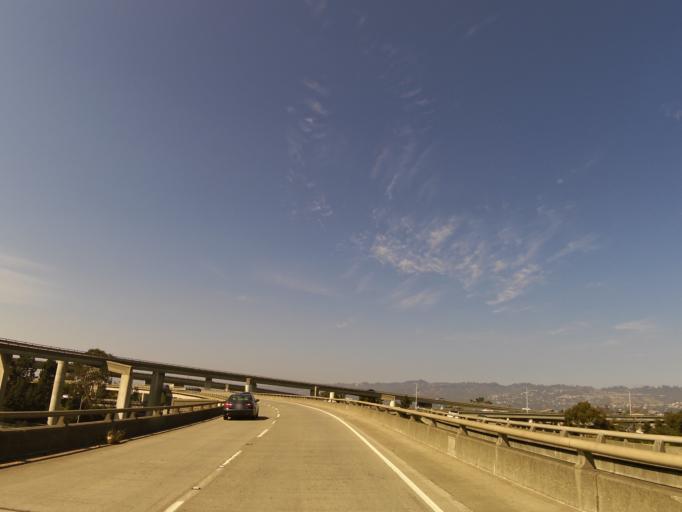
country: US
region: California
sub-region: Alameda County
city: Oakland
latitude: 37.8221
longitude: -122.2685
